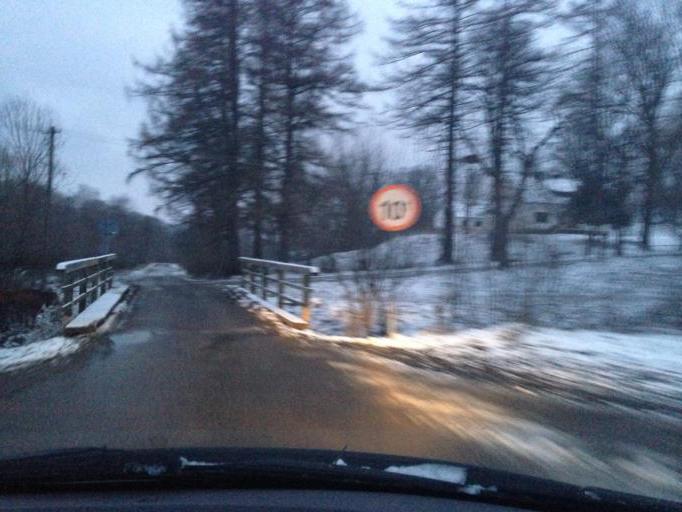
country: PL
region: Subcarpathian Voivodeship
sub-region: Powiat jasielski
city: Krempna
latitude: 49.5289
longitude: 21.5549
